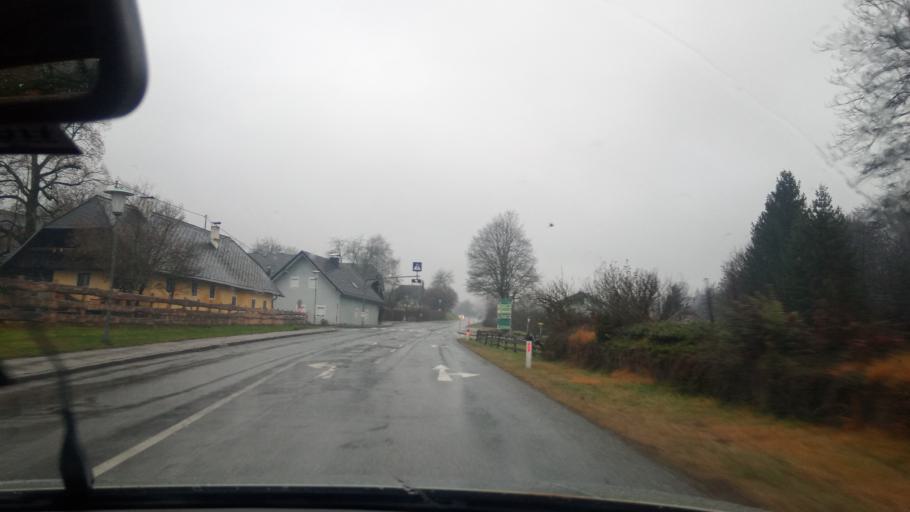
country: AT
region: Carinthia
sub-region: Politischer Bezirk Klagenfurt Land
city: Kottmannsdorf
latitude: 46.5890
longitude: 14.2206
